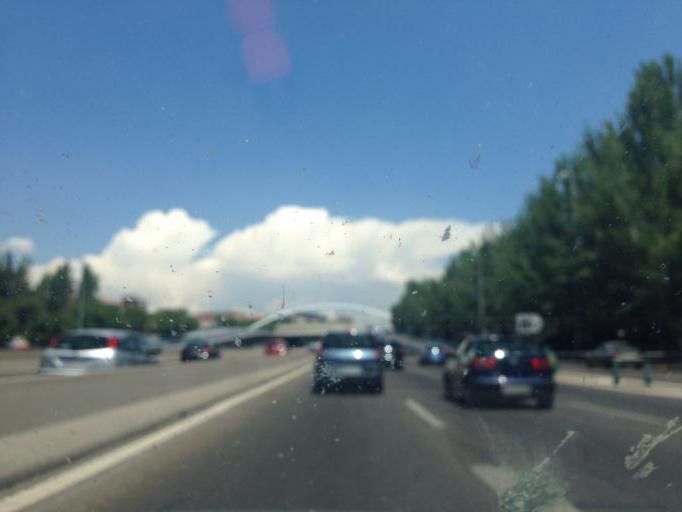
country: ES
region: Madrid
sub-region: Provincia de Madrid
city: Moratalaz
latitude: 40.4280
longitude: -3.6601
